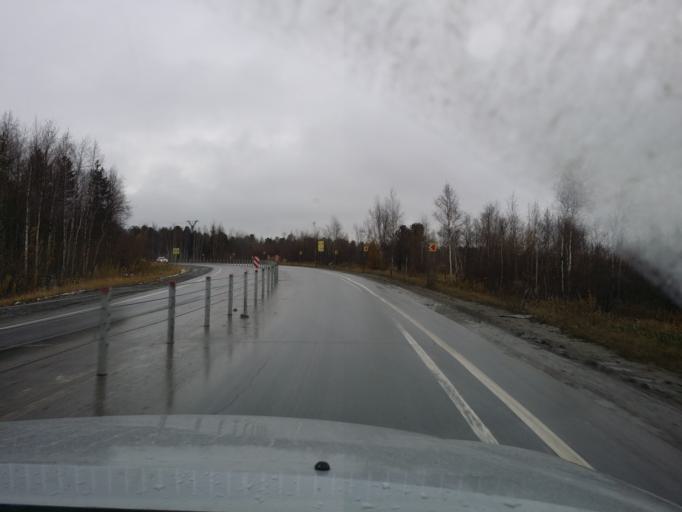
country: RU
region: Khanty-Mansiyskiy Avtonomnyy Okrug
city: Megion
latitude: 61.1099
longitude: 76.0358
